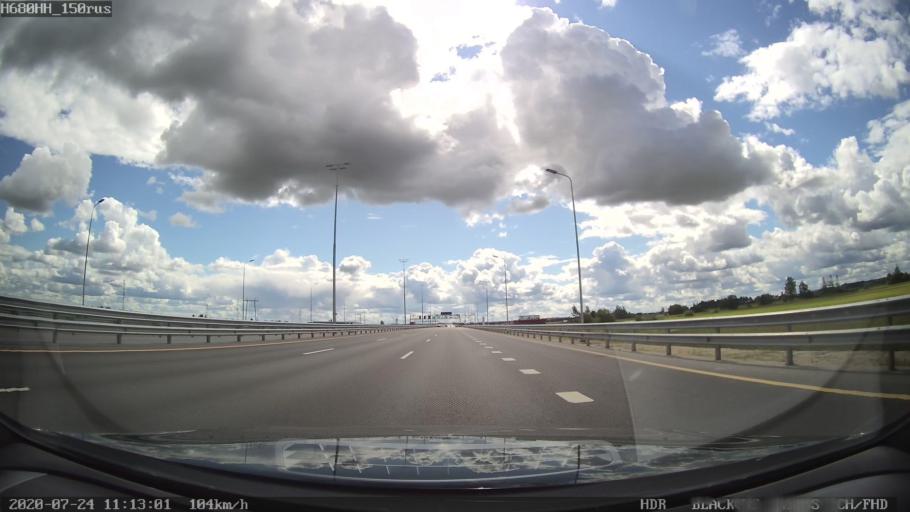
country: RU
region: Leningrad
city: Fedorovskoye
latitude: 59.7043
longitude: 30.5468
